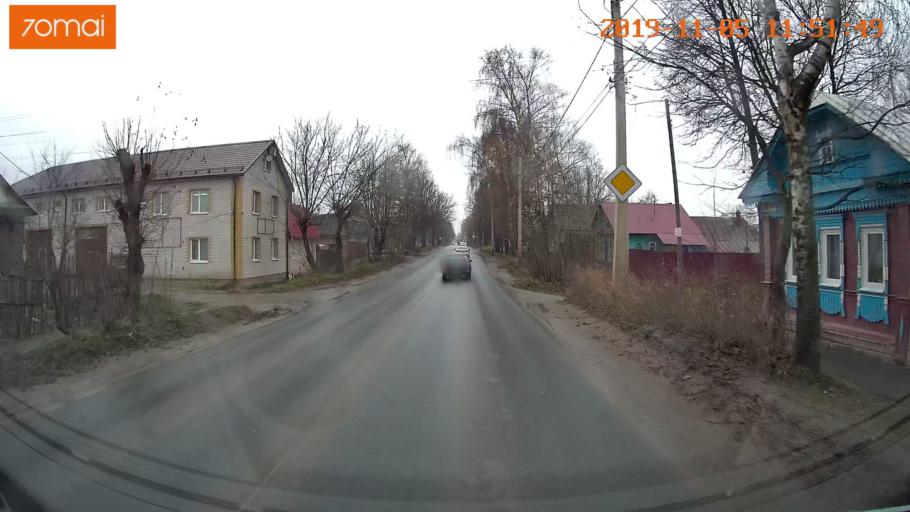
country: RU
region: Ivanovo
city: Bogorodskoye
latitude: 57.0036
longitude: 41.0288
